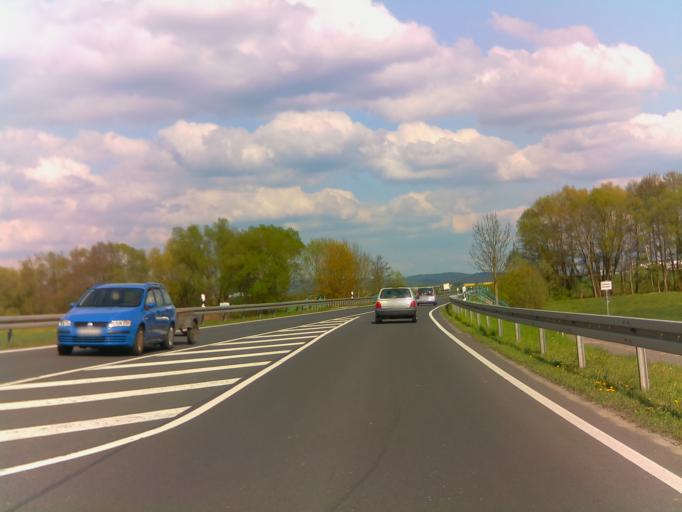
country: DE
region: Bavaria
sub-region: Upper Franconia
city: Ebersdorf
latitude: 50.3194
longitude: 11.1502
